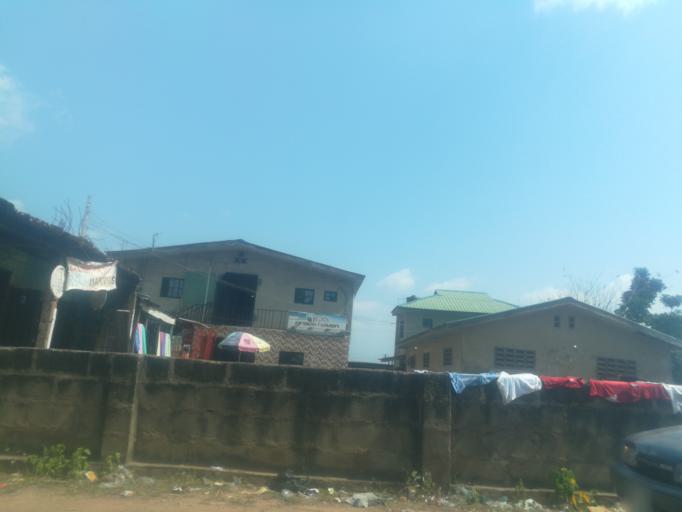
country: NG
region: Oyo
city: Moniya
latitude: 7.4961
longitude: 3.9144
